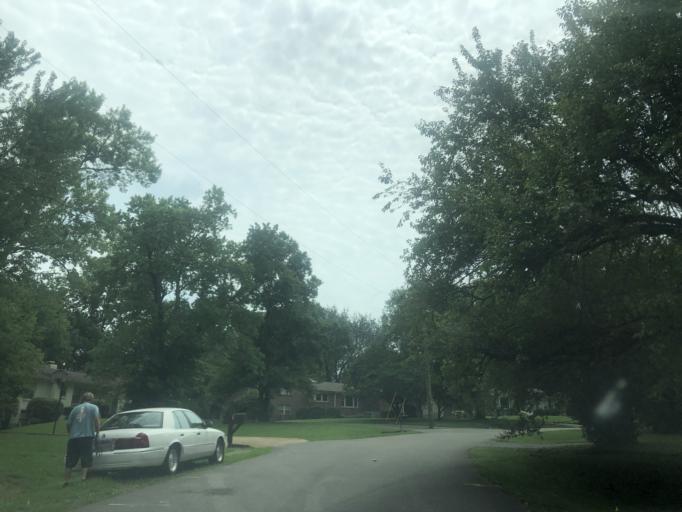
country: US
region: Tennessee
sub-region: Davidson County
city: Oak Hill
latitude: 36.0909
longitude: -86.7919
